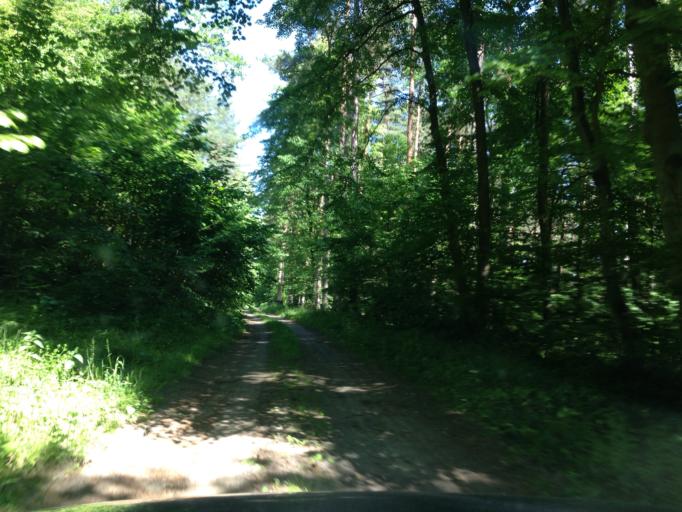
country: PL
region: Kujawsko-Pomorskie
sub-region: Powiat brodnicki
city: Bartniczka
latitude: 53.2652
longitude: 19.5788
